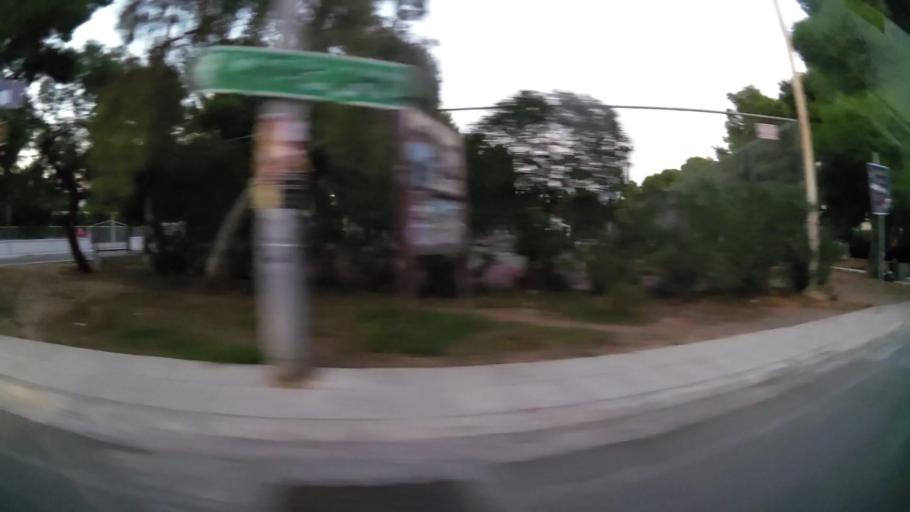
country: GR
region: Attica
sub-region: Nomarchia Anatolikis Attikis
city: Paiania
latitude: 37.9520
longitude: 23.8595
